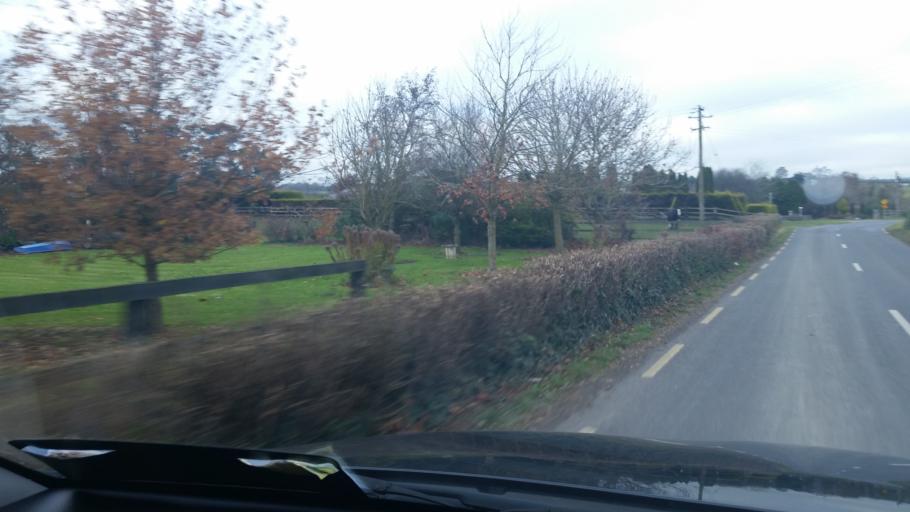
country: IE
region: Leinster
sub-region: Lu
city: Tullyallen
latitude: 53.7192
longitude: -6.4096
